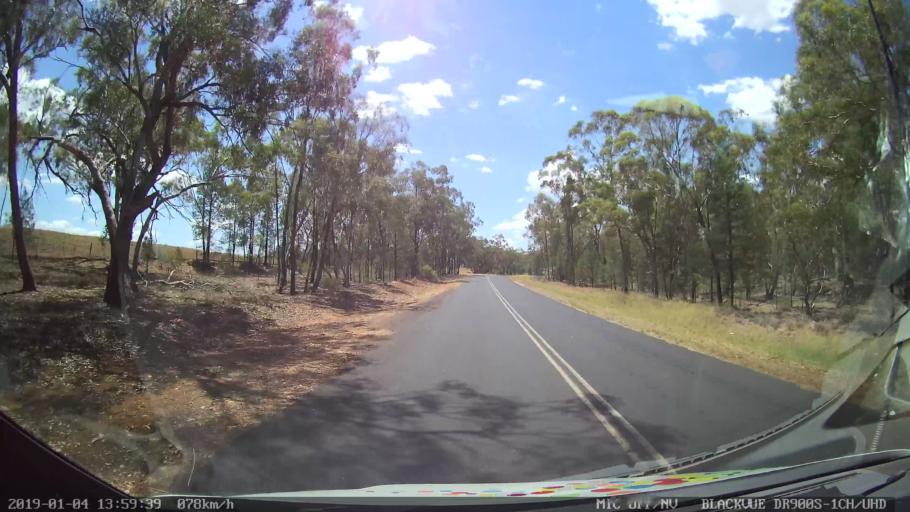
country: AU
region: New South Wales
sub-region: Dubbo Municipality
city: Dubbo
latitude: -32.3146
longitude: 148.5888
